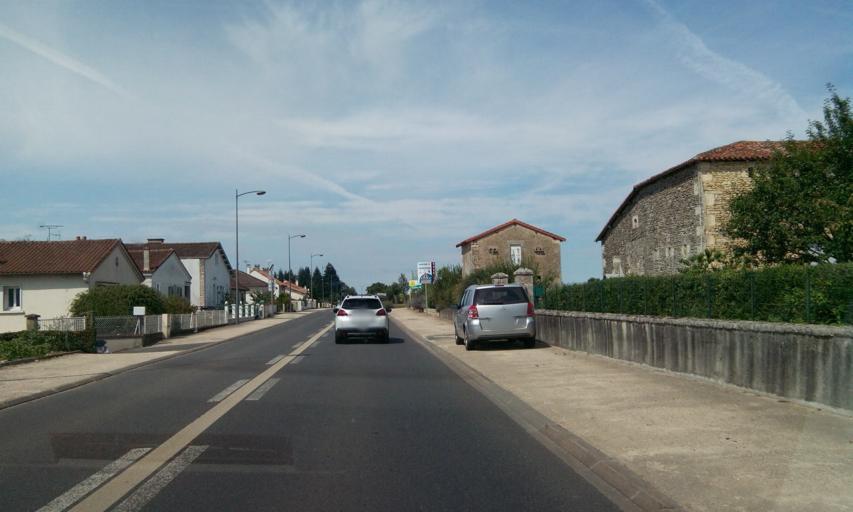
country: FR
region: Poitou-Charentes
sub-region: Departement de la Vienne
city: Civray
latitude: 46.1503
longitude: 0.2673
